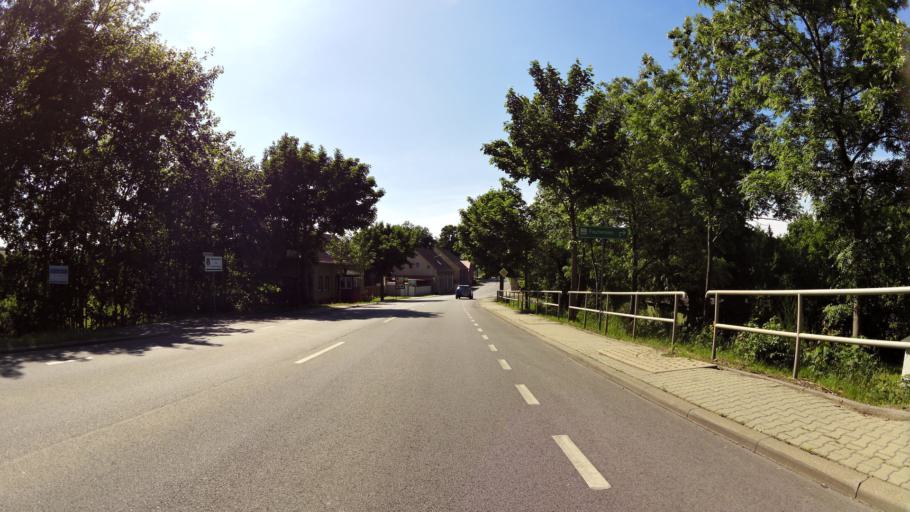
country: DE
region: Brandenburg
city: Frankfurt (Oder)
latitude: 52.3705
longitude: 14.4846
